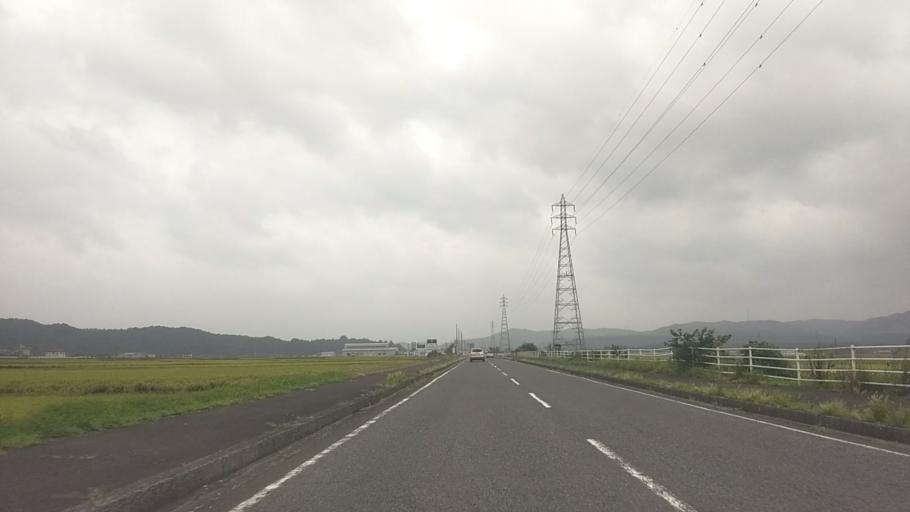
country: JP
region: Chiba
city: Kisarazu
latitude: 35.3354
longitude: 140.0549
